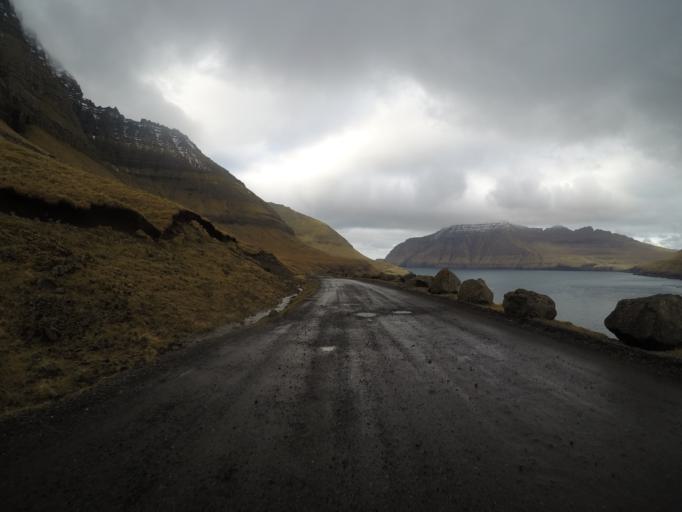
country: FO
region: Nordoyar
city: Klaksvik
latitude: 62.3376
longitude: -6.5790
